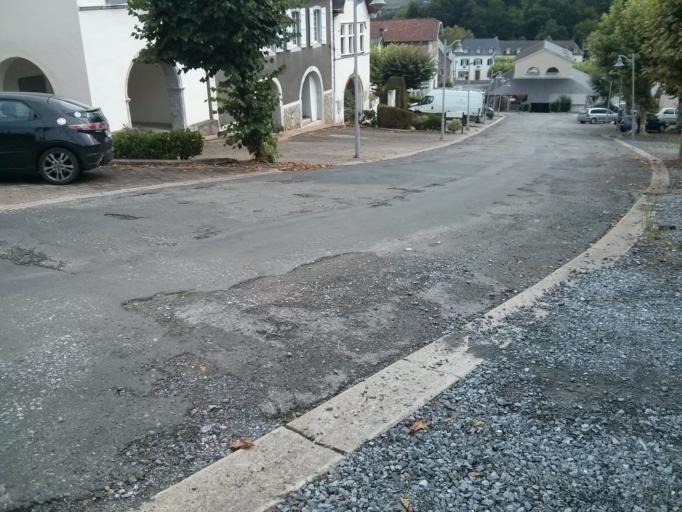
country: FR
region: Aquitaine
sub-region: Departement des Pyrenees-Atlantiques
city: Mauleon-Licharre
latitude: 43.2209
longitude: -0.8851
